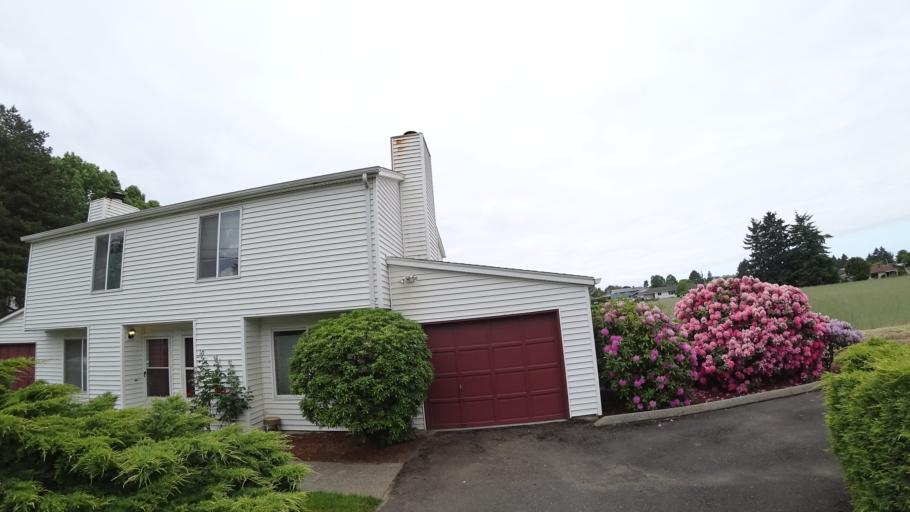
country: US
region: Oregon
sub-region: Multnomah County
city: Fairview
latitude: 45.5492
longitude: -122.5110
